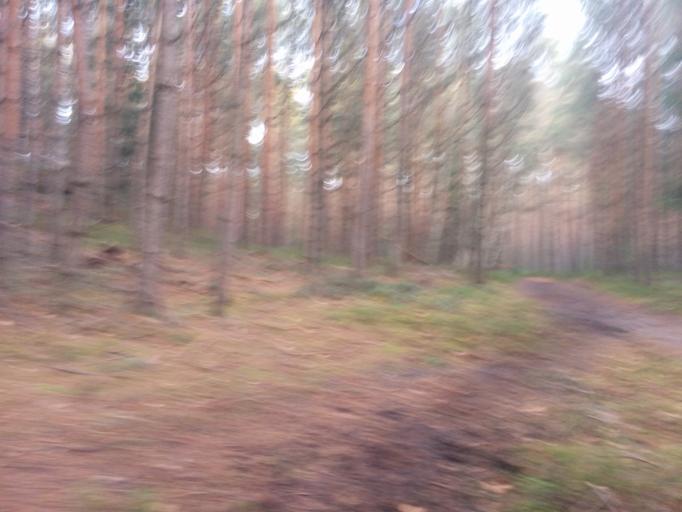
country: CZ
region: Central Bohemia
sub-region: Okres Mlada Boleslav
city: Zd'ar
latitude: 50.5231
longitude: 15.1188
